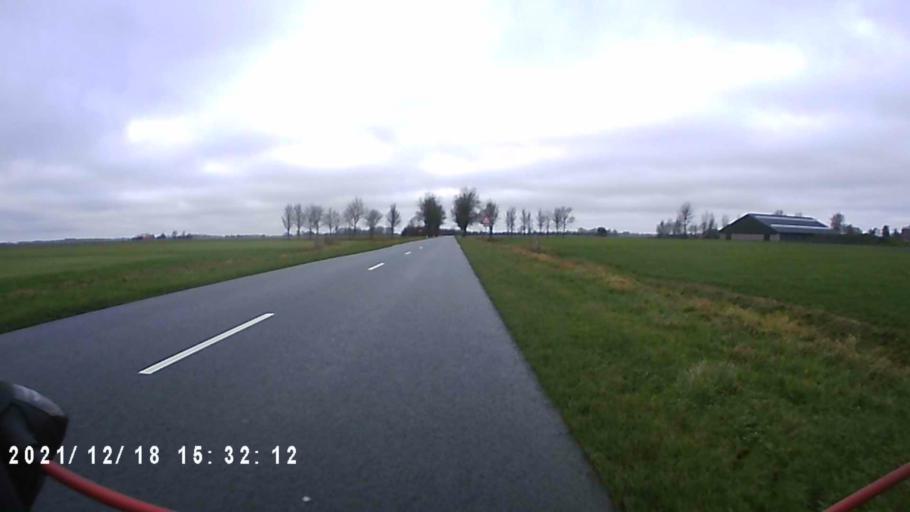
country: NL
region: Friesland
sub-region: Gemeente Dongeradeel
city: Anjum
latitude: 53.3413
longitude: 6.1352
